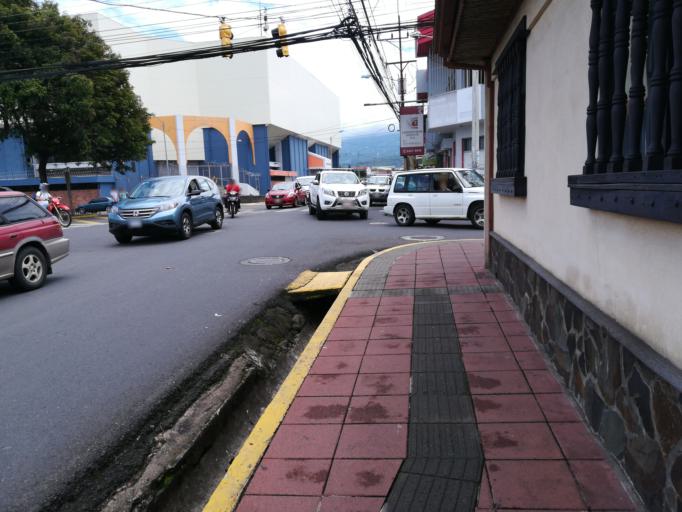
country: CR
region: Heredia
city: Heredia
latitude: 9.9983
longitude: -84.1217
